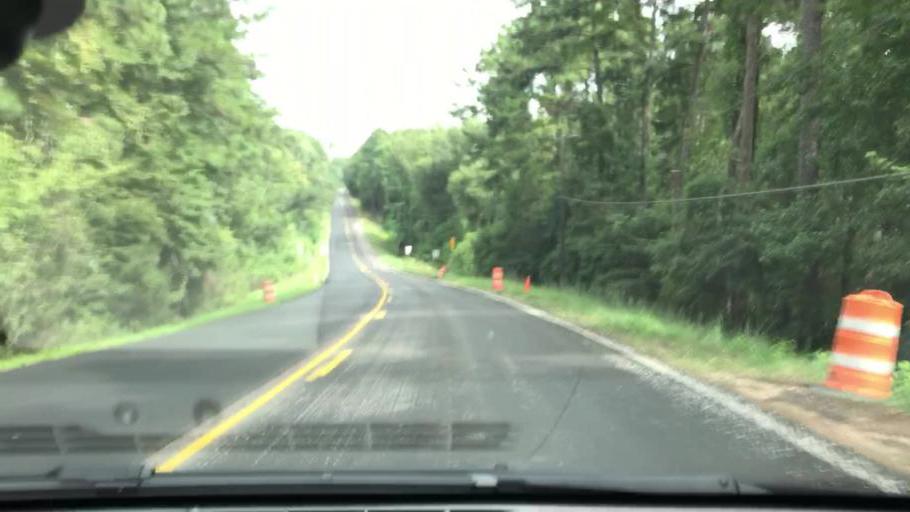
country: US
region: Georgia
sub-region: Clay County
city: Fort Gaines
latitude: 31.5964
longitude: -85.0443
